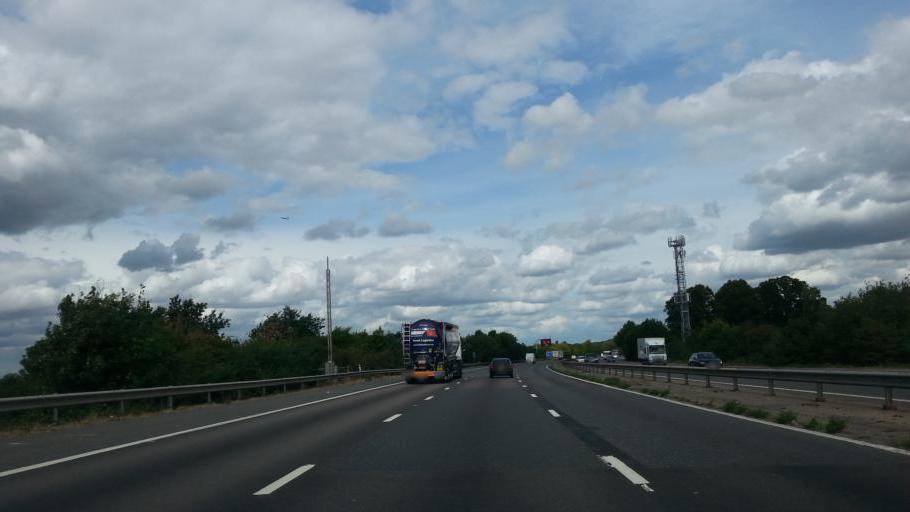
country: GB
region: England
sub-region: Essex
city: Little Hallingbury
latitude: 51.8227
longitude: 0.1853
